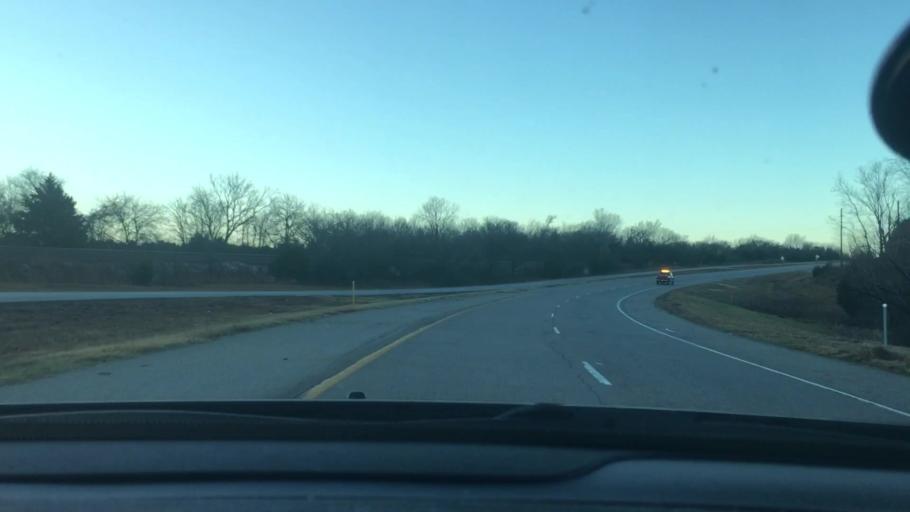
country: US
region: Oklahoma
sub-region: Pontotoc County
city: Ada
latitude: 34.7320
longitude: -96.7089
